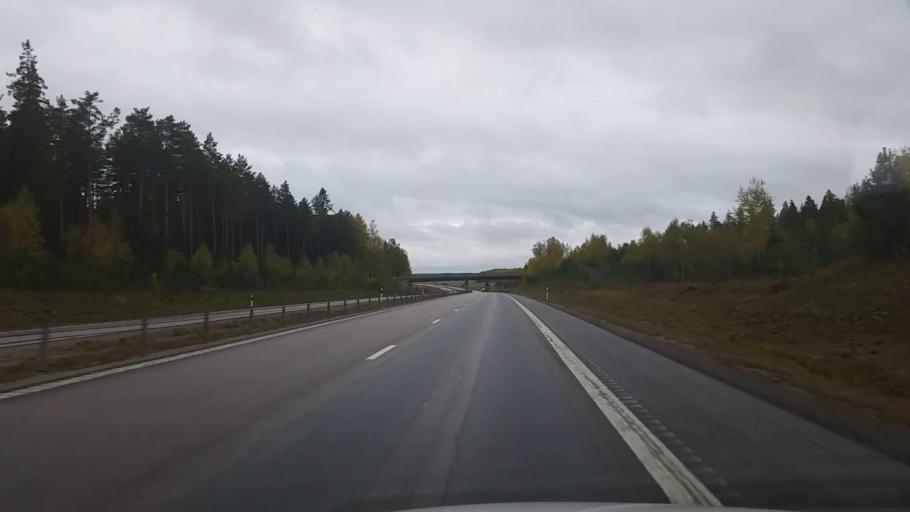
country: SE
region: Uppsala
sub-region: Osthammars Kommun
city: Bjorklinge
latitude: 60.1352
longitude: 17.5473
